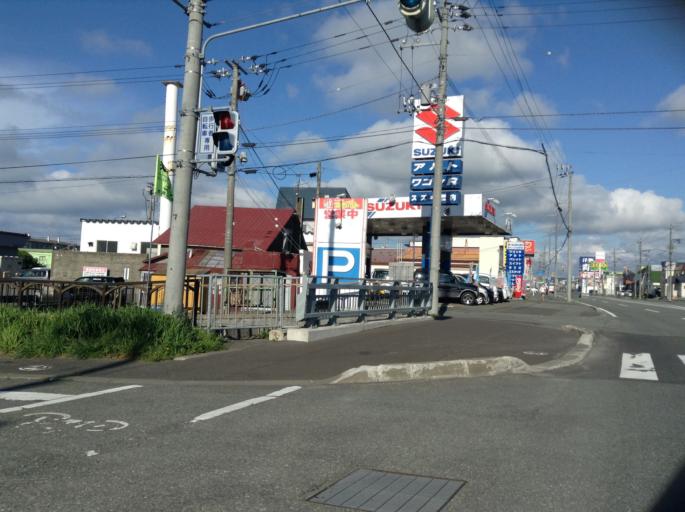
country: JP
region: Hokkaido
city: Wakkanai
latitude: 45.3965
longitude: 141.6957
